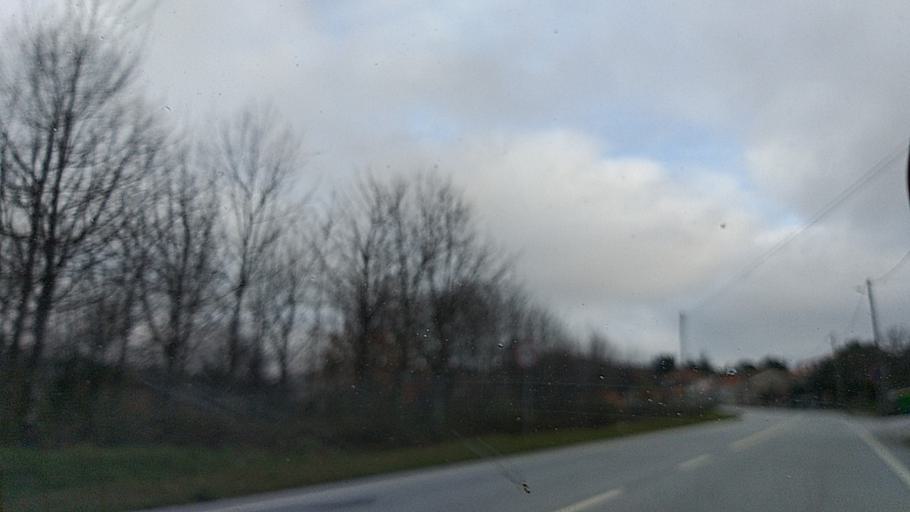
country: PT
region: Guarda
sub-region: Fornos de Algodres
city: Fornos de Algodres
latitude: 40.6530
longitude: -7.4869
